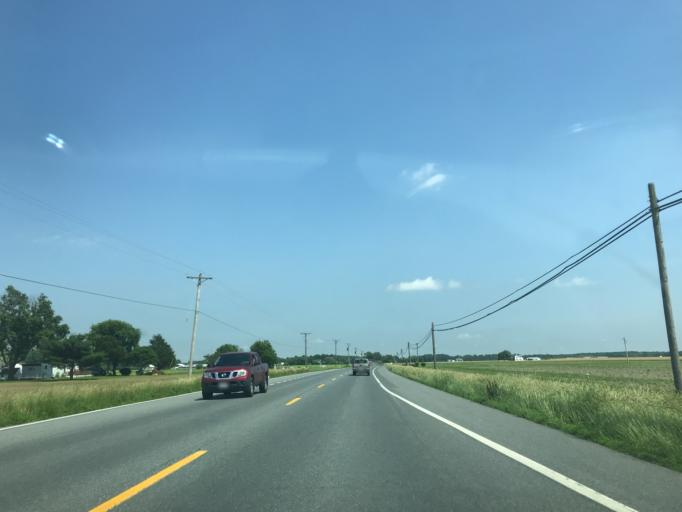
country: US
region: Maryland
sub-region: Dorchester County
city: Hurlock
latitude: 38.5821
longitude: -75.8513
